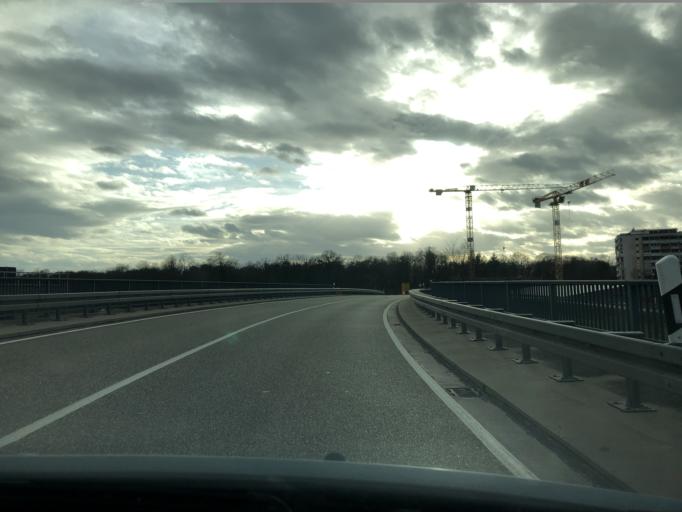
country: DE
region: Baden-Wuerttemberg
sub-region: Freiburg Region
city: Umkirch
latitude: 48.0288
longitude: 7.7796
